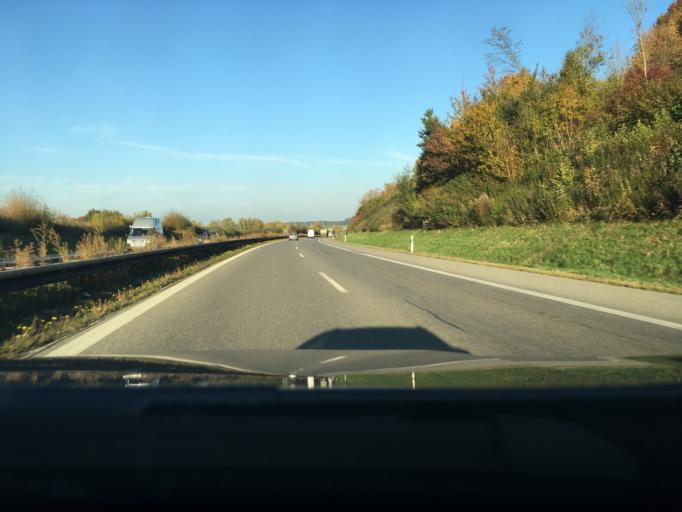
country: DE
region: Baden-Wuerttemberg
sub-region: Tuebingen Region
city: Aichstetten
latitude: 47.8953
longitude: 10.0497
